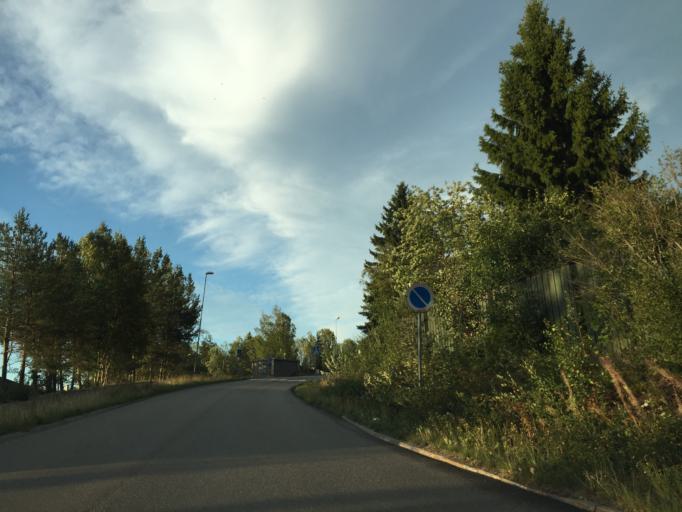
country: NO
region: Akershus
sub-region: Ski
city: Ski
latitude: 59.7636
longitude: 10.8472
